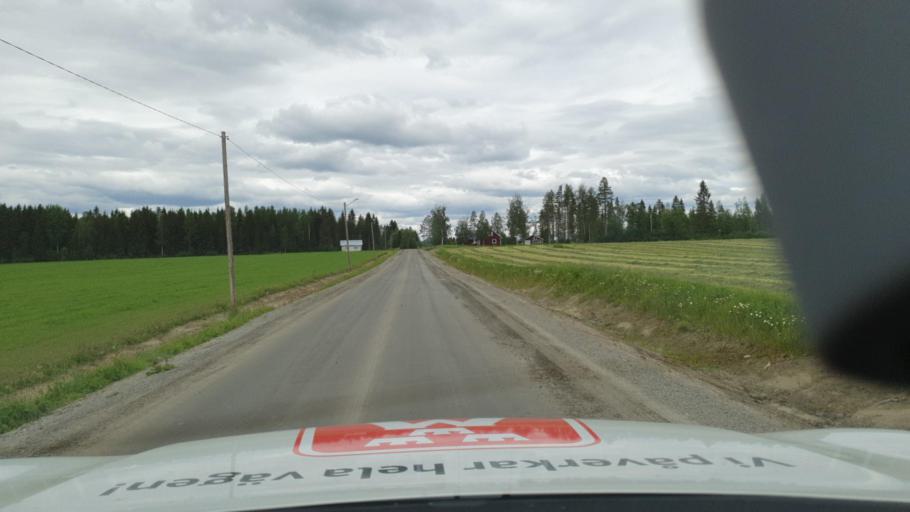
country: SE
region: Vaesterbotten
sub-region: Nordmalings Kommun
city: Nordmaling
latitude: 63.7004
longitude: 19.4421
